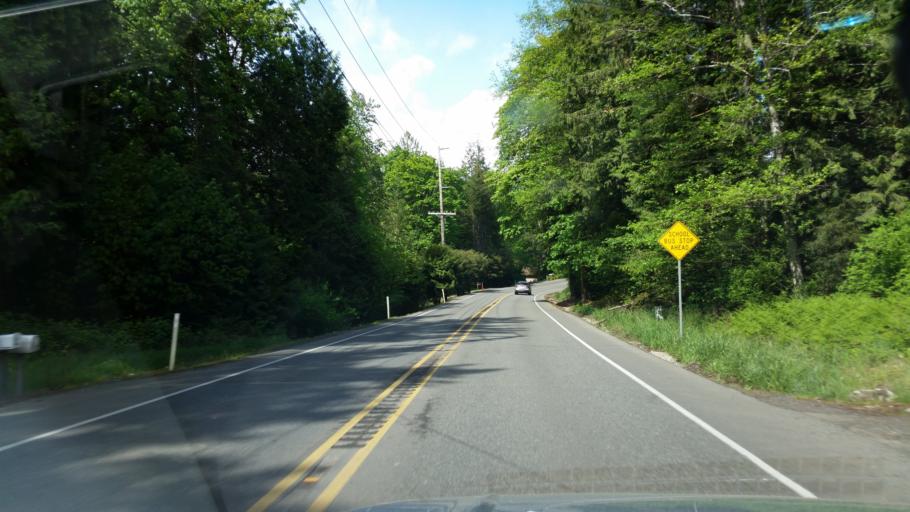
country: US
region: Washington
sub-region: Mason County
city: Belfair
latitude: 47.4221
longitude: -122.8472
